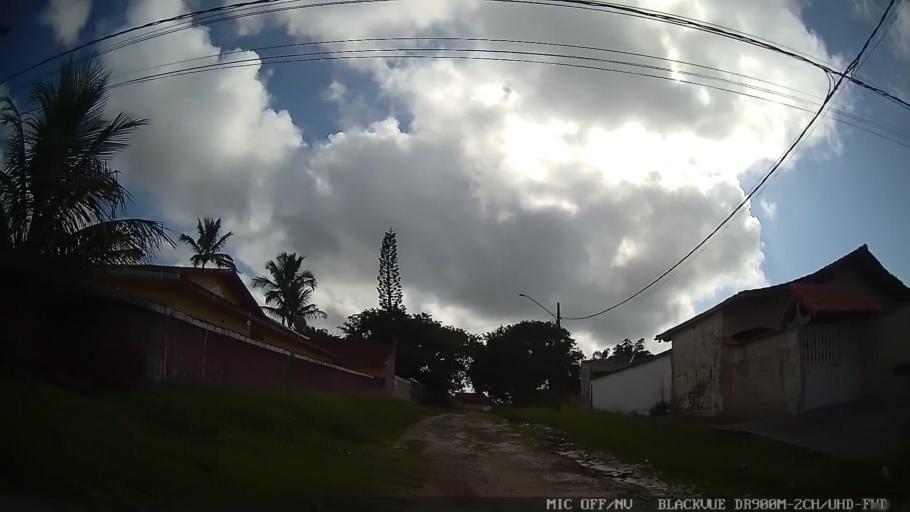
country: BR
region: Sao Paulo
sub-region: Peruibe
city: Peruibe
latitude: -24.2716
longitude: -46.9442
